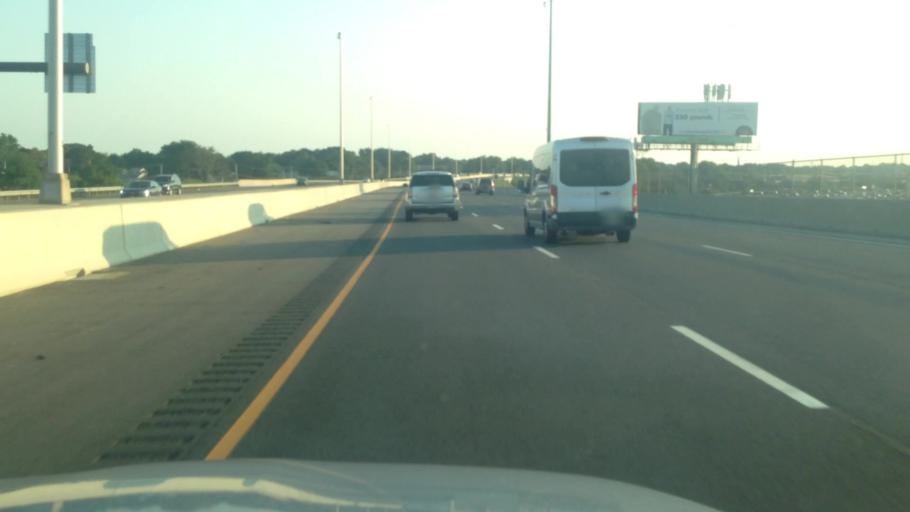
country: US
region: Connecticut
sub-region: Fairfield County
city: Stratford
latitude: 41.2016
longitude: -73.1139
